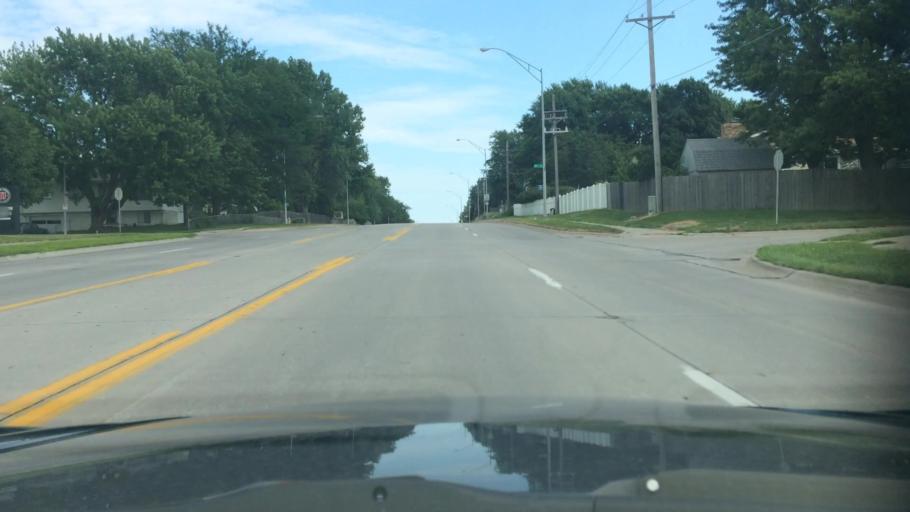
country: US
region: Nebraska
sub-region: Douglas County
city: Ralston
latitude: 41.2053
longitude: -96.0795
